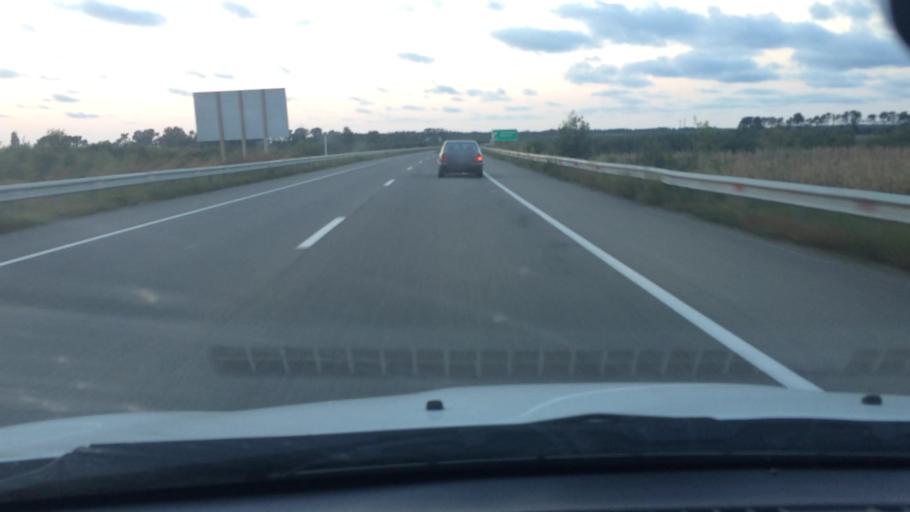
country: GE
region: Guria
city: Urek'i
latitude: 41.9104
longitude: 41.7826
